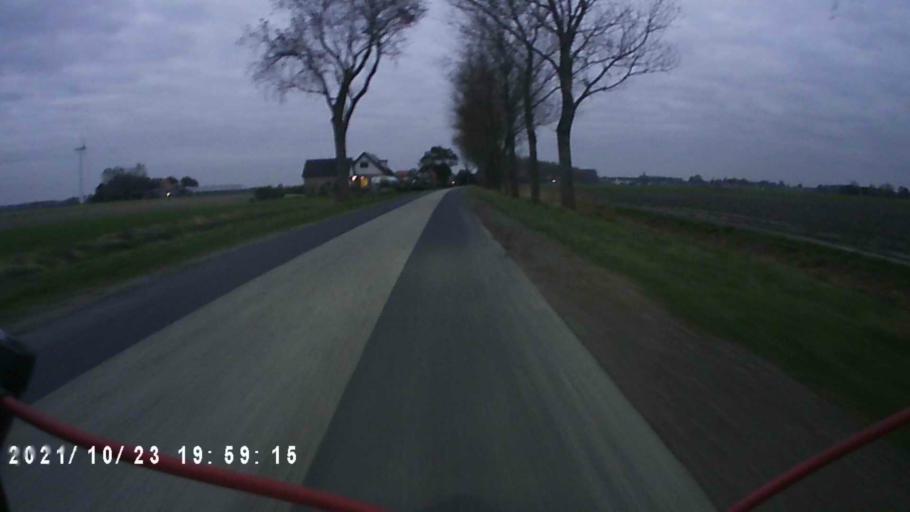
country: NL
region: Friesland
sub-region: Gemeente Harlingen
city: Harlingen
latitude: 53.1112
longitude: 5.4561
